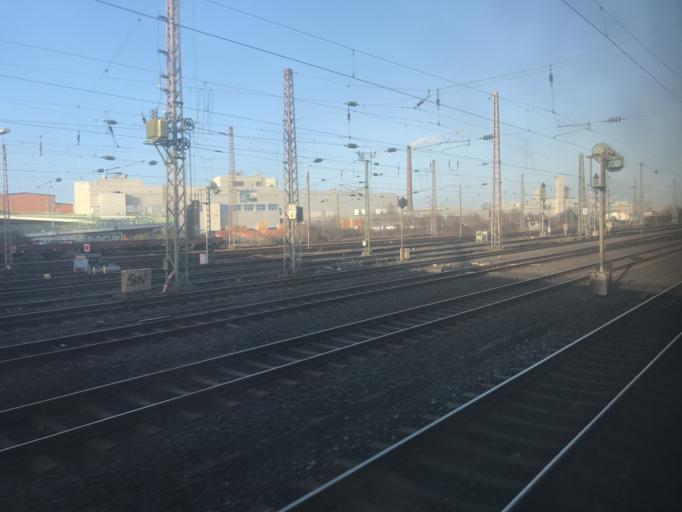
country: DE
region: North Rhine-Westphalia
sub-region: Regierungsbezirk Dusseldorf
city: Dusseldorf
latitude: 51.2533
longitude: 6.7933
